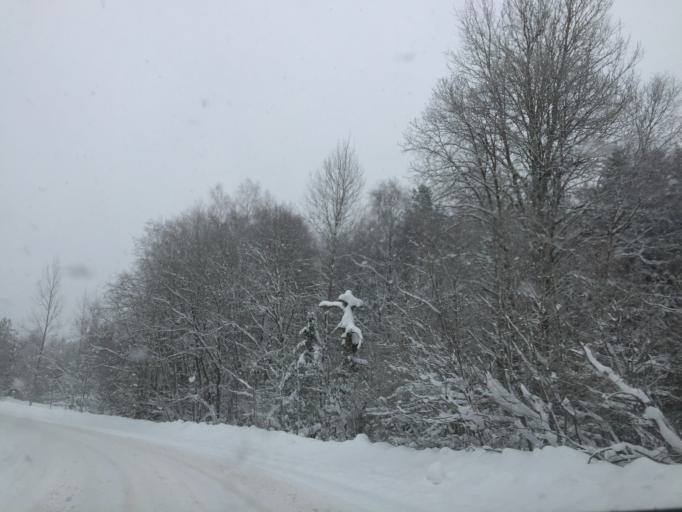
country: LV
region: Amatas Novads
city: Drabesi
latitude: 57.0834
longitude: 25.3684
